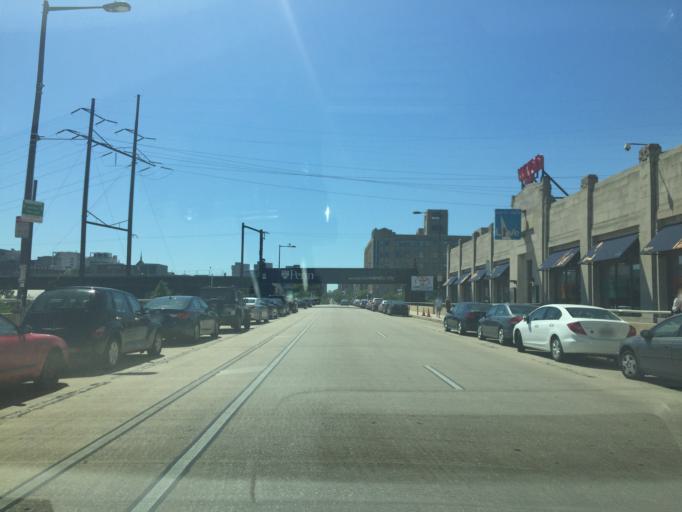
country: US
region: Pennsylvania
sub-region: Philadelphia County
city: Philadelphia
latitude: 39.9519
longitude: -75.1846
